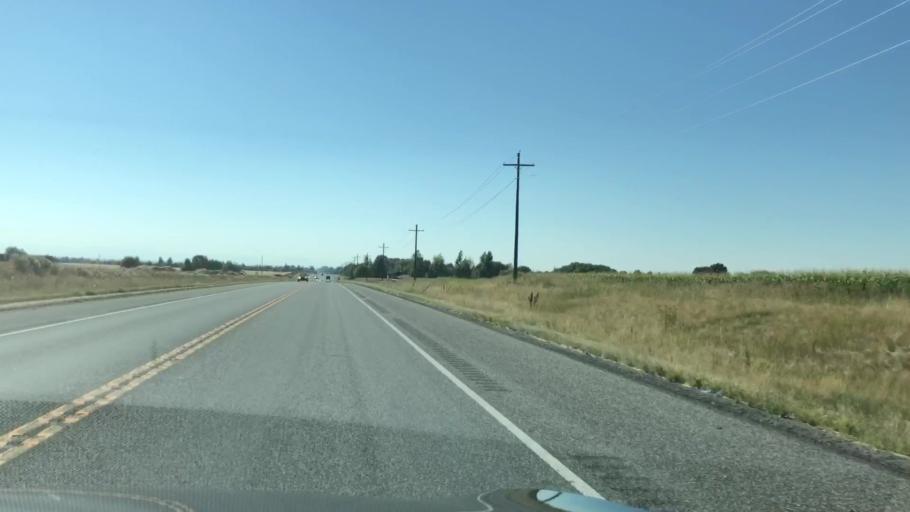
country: US
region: Montana
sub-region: Gallatin County
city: Belgrade
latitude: 45.7291
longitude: -111.1086
